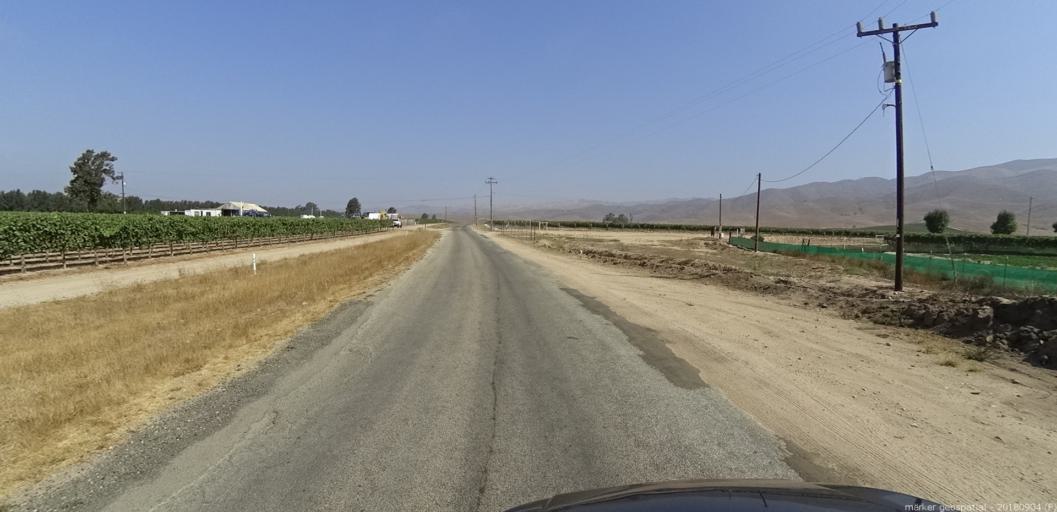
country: US
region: California
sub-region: Monterey County
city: Soledad
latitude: 36.4734
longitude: -121.3497
